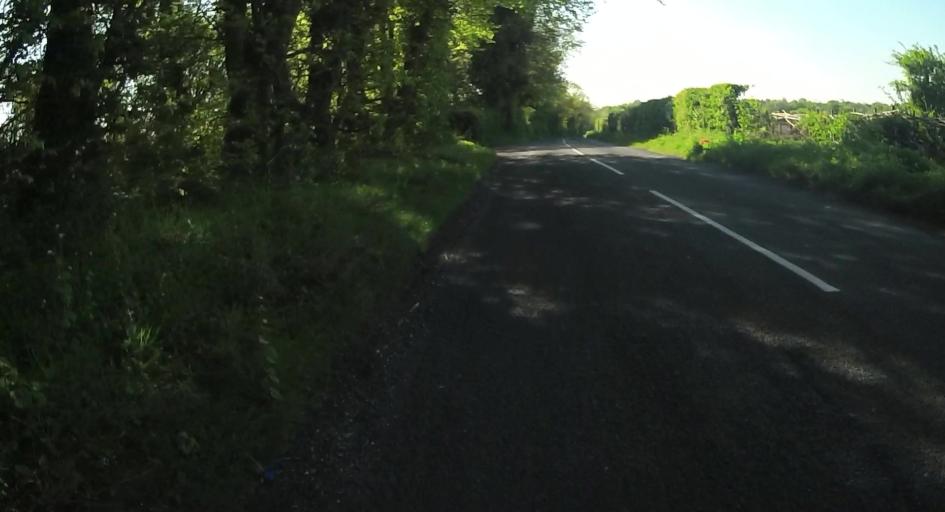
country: GB
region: England
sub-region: Hampshire
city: Old Basing
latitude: 51.2478
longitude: -1.0510
